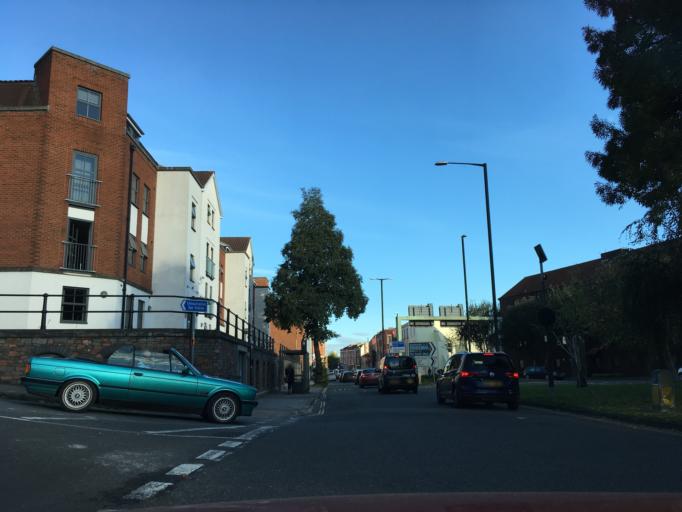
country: GB
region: England
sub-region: Bristol
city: Bristol
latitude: 51.4502
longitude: -2.6175
